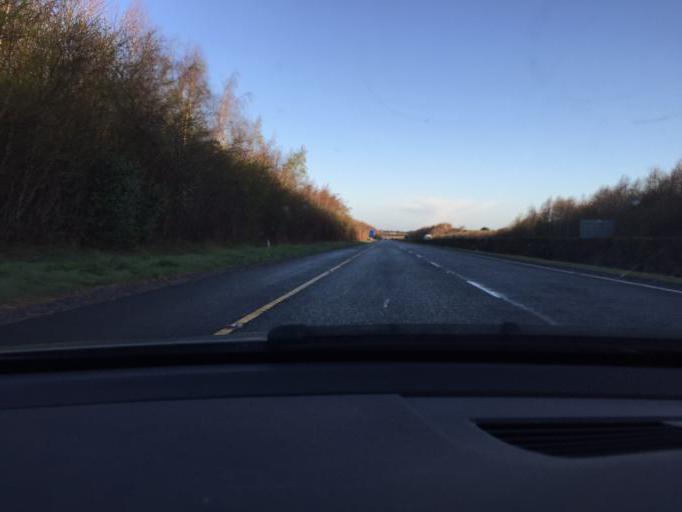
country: IE
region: Leinster
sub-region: Lu
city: Dunleer
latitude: 53.8437
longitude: -6.4200
